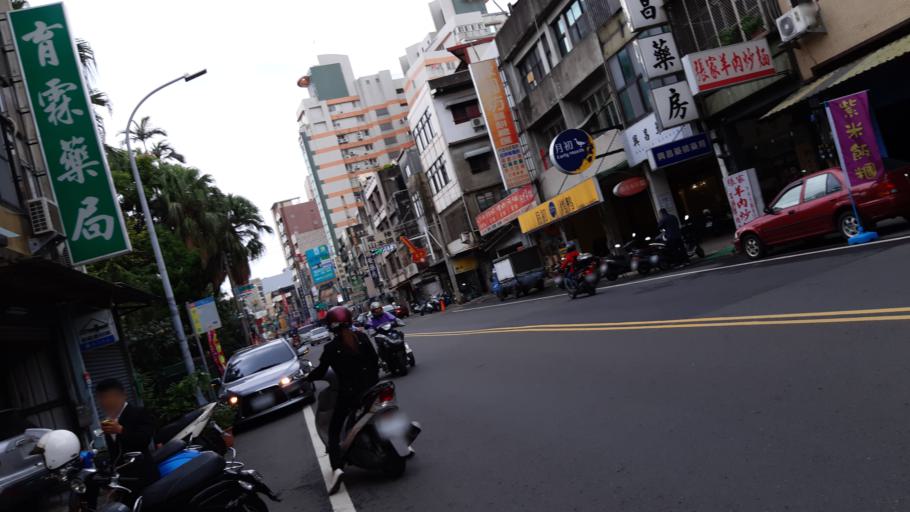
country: TW
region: Taiwan
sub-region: Hsinchu
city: Hsinchu
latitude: 24.8009
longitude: 120.9591
